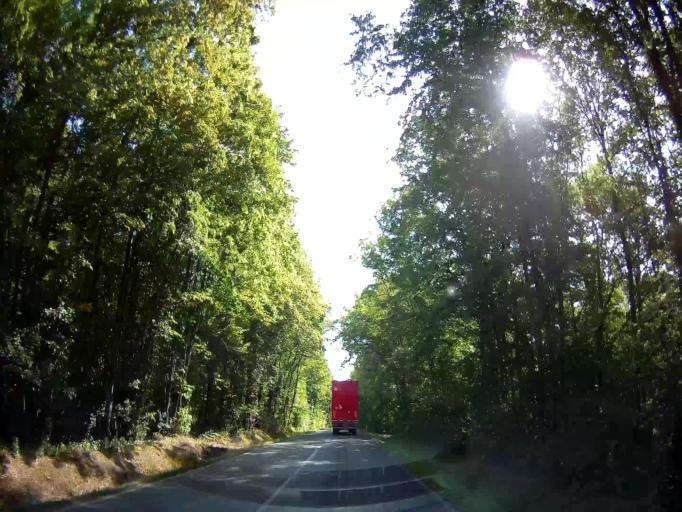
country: BE
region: Wallonia
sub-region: Province de Namur
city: Rochefort
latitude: 50.1676
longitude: 5.1605
